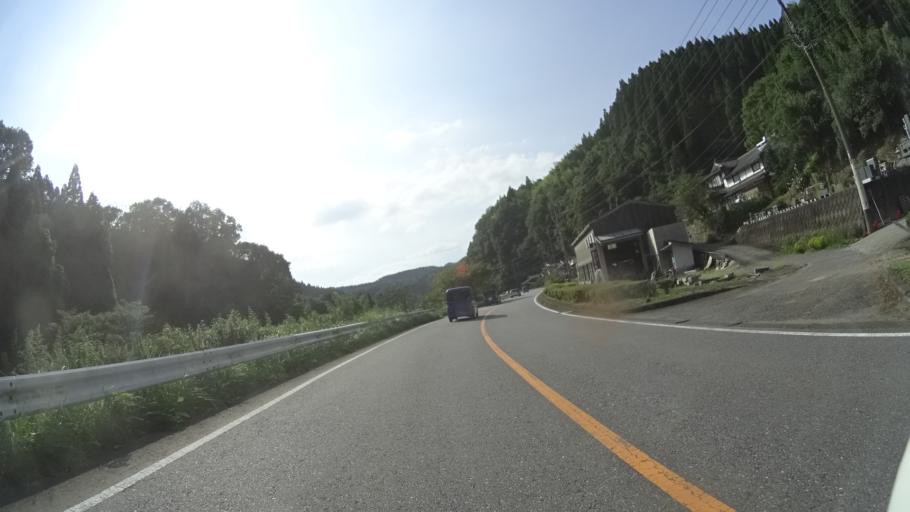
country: JP
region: Kumamoto
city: Aso
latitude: 32.6849
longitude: 131.0518
